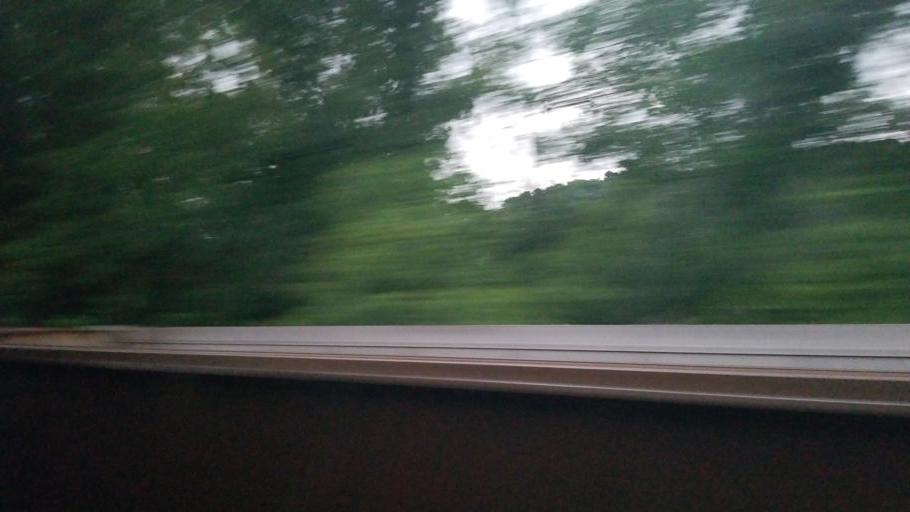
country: US
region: Pennsylvania
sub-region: Allegheny County
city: Edgeworth
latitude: 40.5511
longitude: -80.2004
